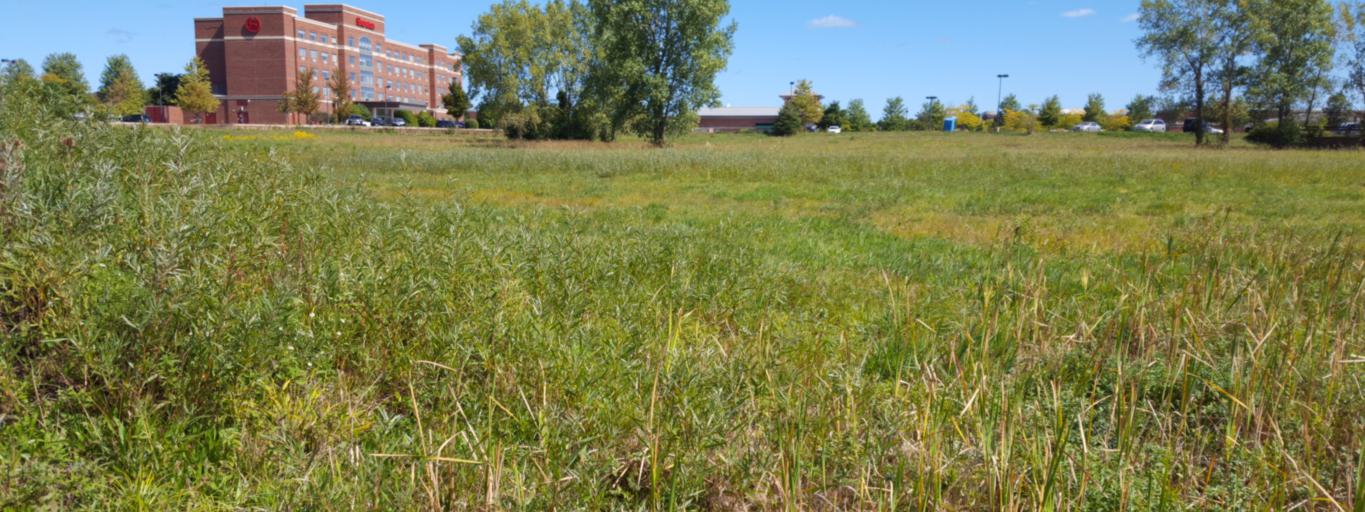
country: US
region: Illinois
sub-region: Cook County
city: Northbrook
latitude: 42.1073
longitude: -87.8096
